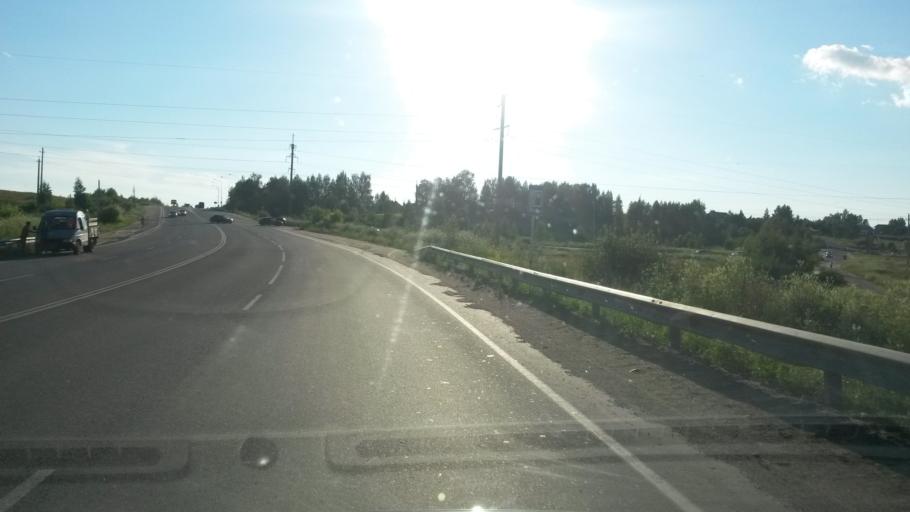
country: RU
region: Ivanovo
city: Novo-Talitsy
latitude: 57.0217
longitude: 40.9092
